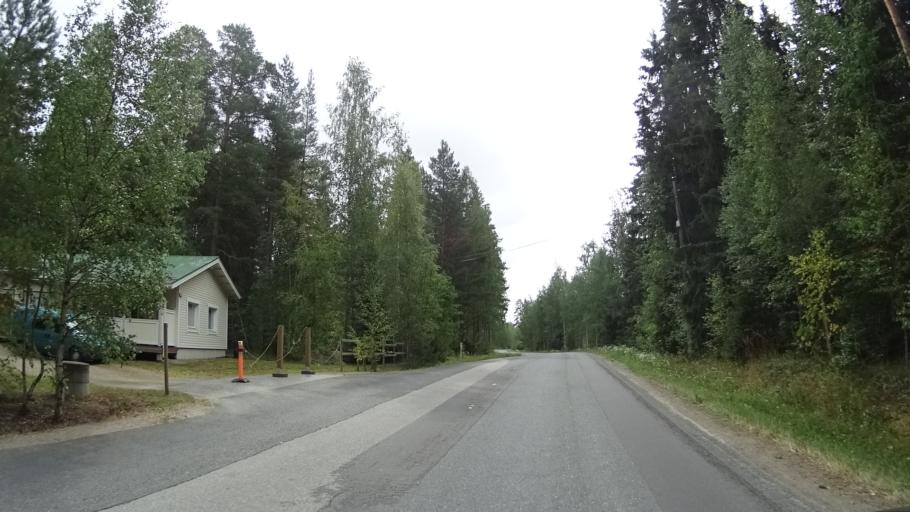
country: FI
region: Pirkanmaa
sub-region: Tampere
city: Kangasala
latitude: 61.4507
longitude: 24.1180
